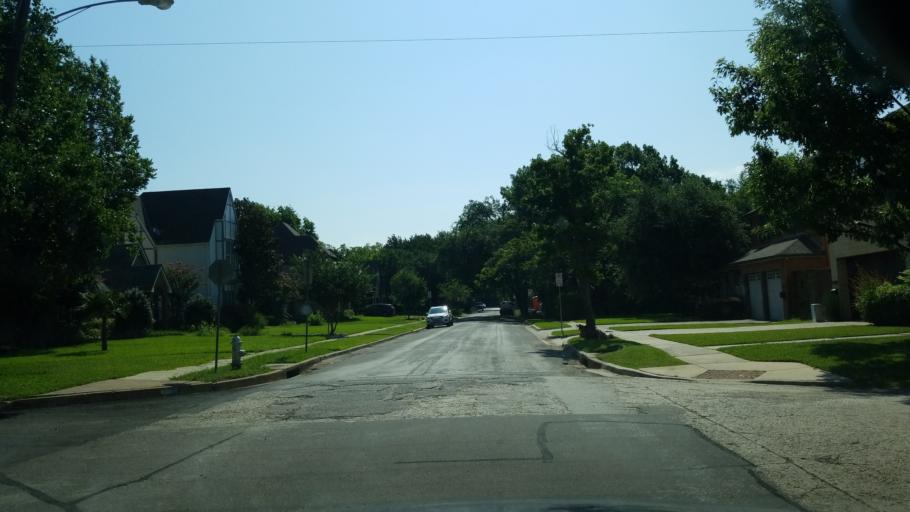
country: US
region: Texas
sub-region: Dallas County
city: Highland Park
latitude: 32.8327
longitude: -96.7723
